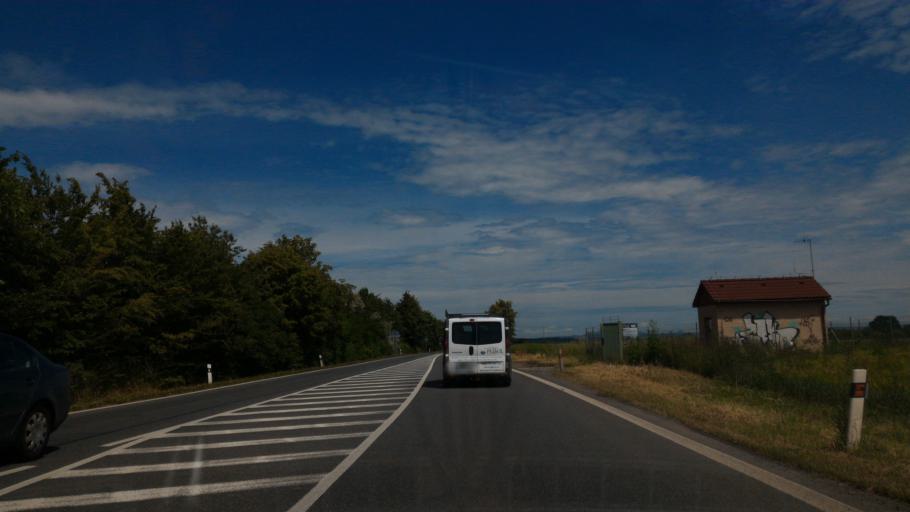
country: CZ
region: Central Bohemia
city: Libeznice
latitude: 50.2022
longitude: 14.4981
